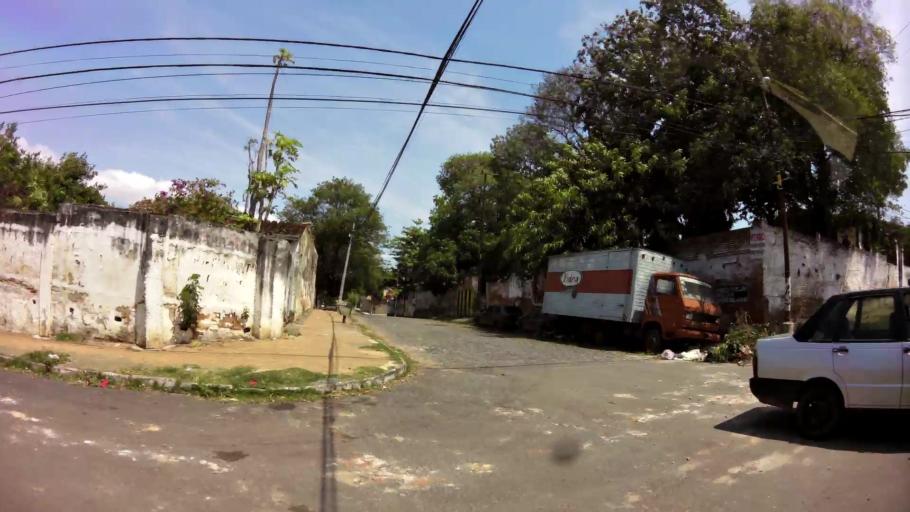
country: PY
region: Presidente Hayes
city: Nanawa
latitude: -25.2807
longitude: -57.6487
